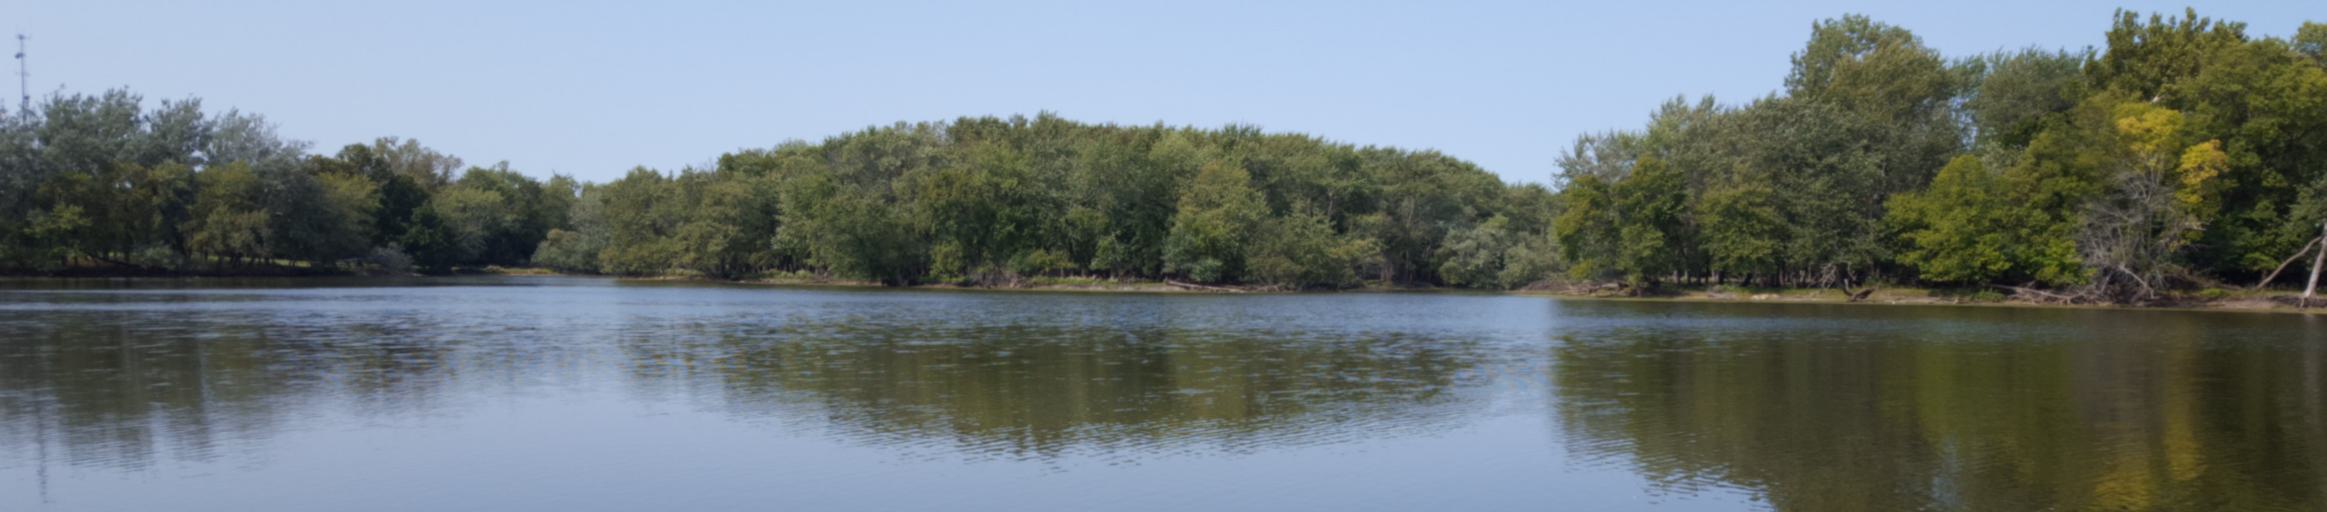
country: US
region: Illinois
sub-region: Cook County
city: Northfield
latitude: 42.1023
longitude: -87.7604
